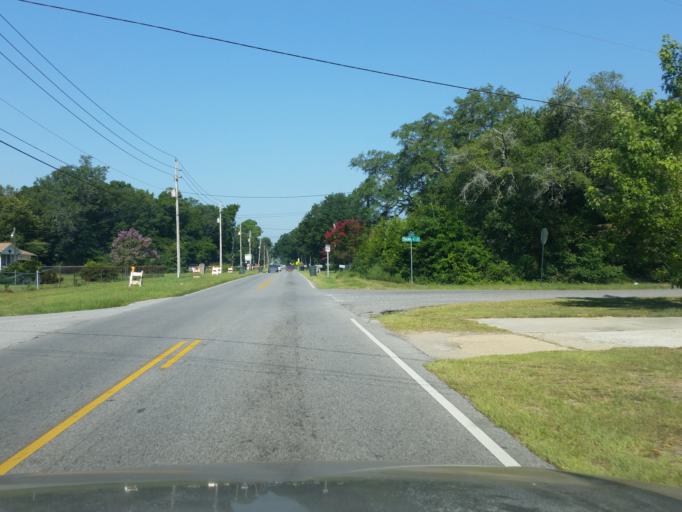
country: US
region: Florida
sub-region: Escambia County
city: Ensley
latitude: 30.5175
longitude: -87.2464
